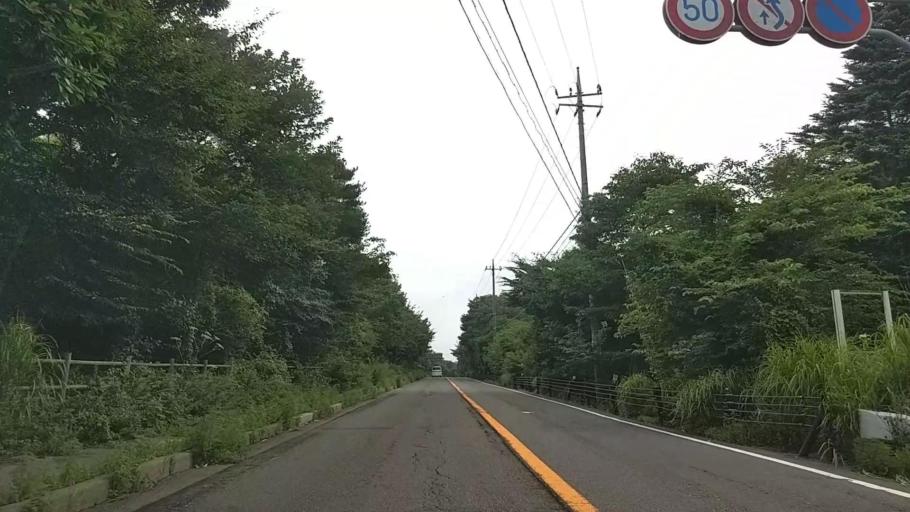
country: JP
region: Yamanashi
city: Fujikawaguchiko
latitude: 35.4496
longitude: 138.6081
